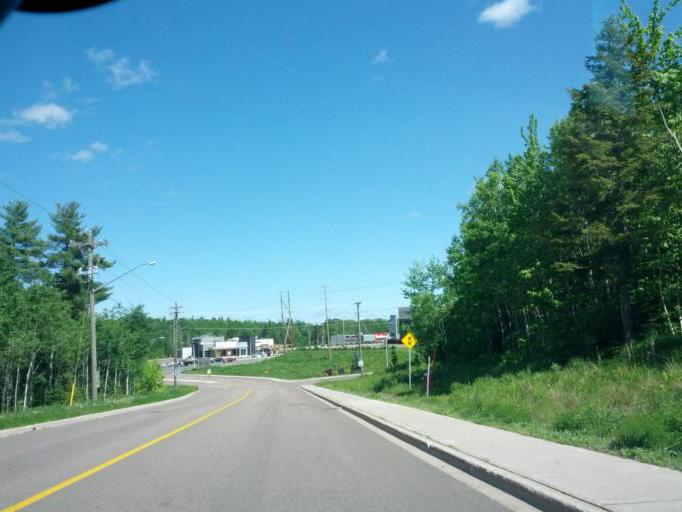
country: CA
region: New Brunswick
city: Moncton
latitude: 46.1217
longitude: -64.8320
